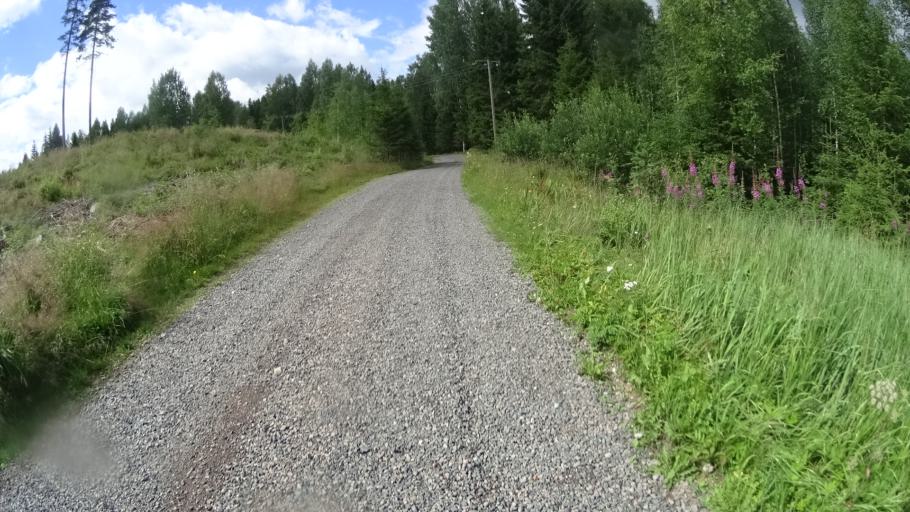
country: FI
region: Uusimaa
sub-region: Helsinki
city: Karkkila
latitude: 60.6053
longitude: 24.2001
